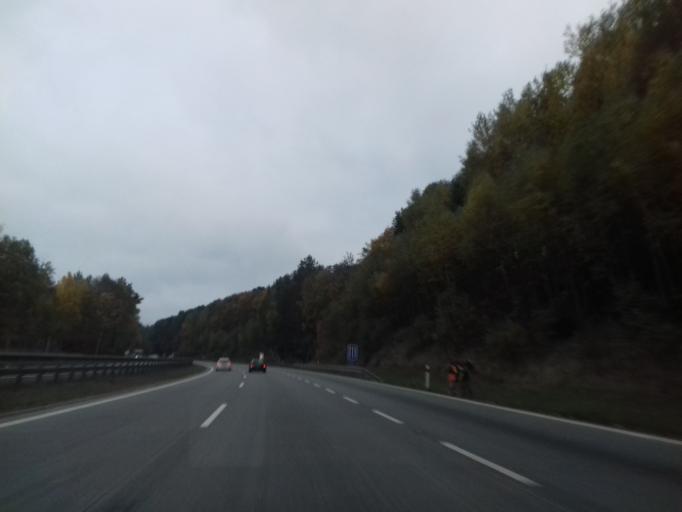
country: CZ
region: Central Bohemia
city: Vlasim
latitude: 49.7636
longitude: 14.9515
